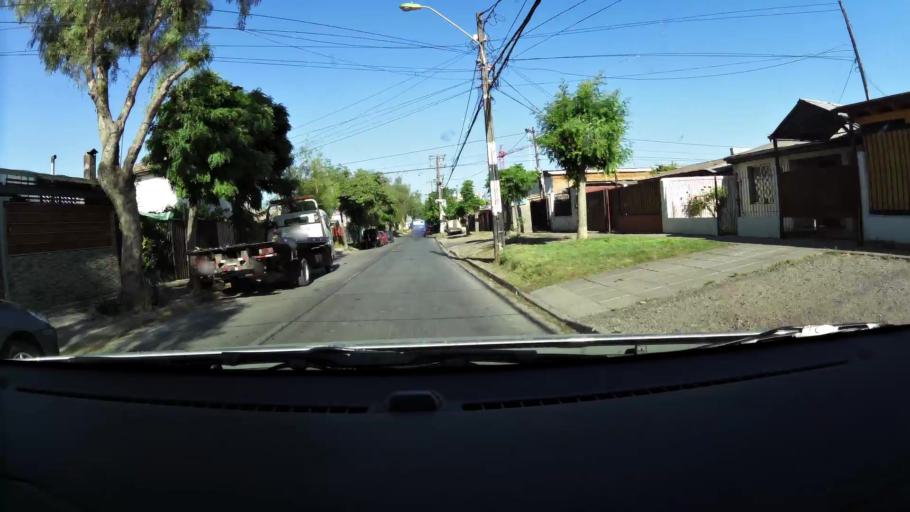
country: CL
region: Santiago Metropolitan
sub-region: Provincia de Maipo
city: San Bernardo
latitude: -33.5468
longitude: -70.6848
